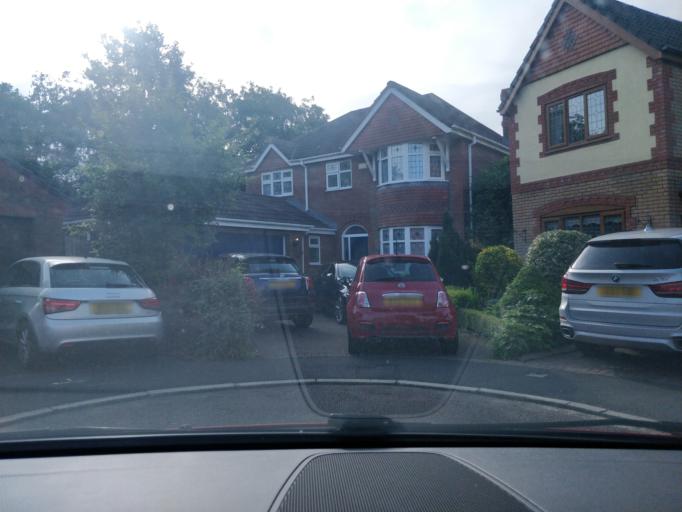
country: GB
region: England
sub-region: Lancashire
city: Banks
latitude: 53.6738
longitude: -2.9120
